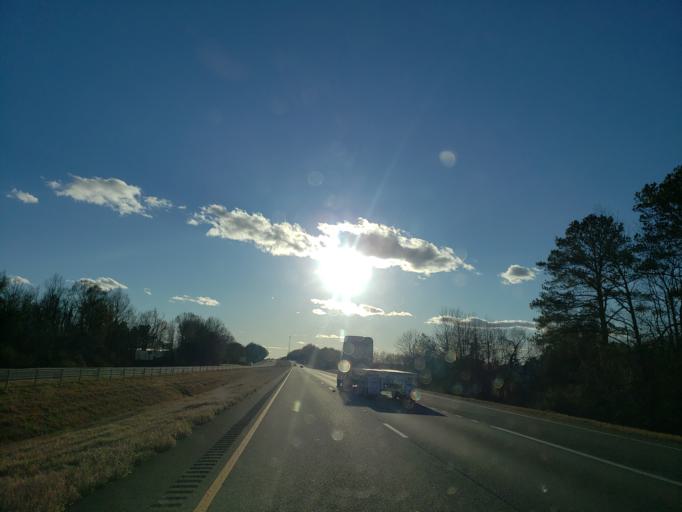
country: US
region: Alabama
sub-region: Greene County
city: Eutaw
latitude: 32.7952
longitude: -88.0338
